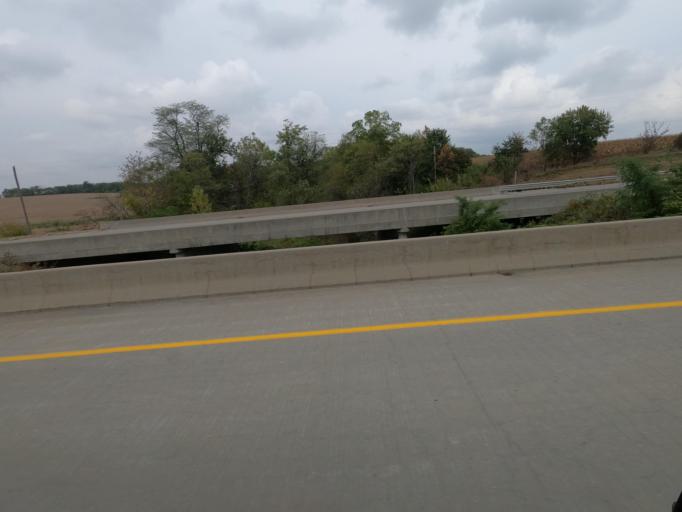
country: US
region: Iowa
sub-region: Wapello County
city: Eddyville
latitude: 41.1200
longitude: -92.5541
